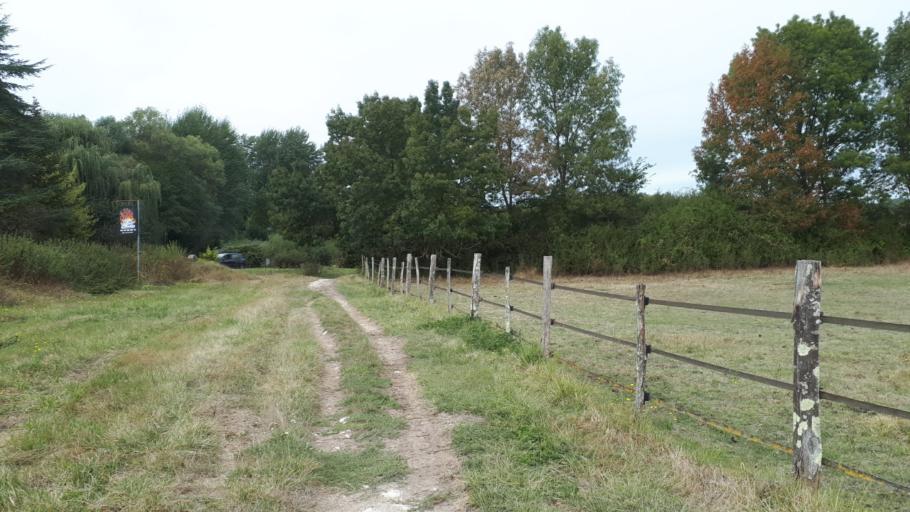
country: FR
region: Centre
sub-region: Departement du Loir-et-Cher
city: Saint-Gervais-la-Foret
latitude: 47.5672
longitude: 1.3464
